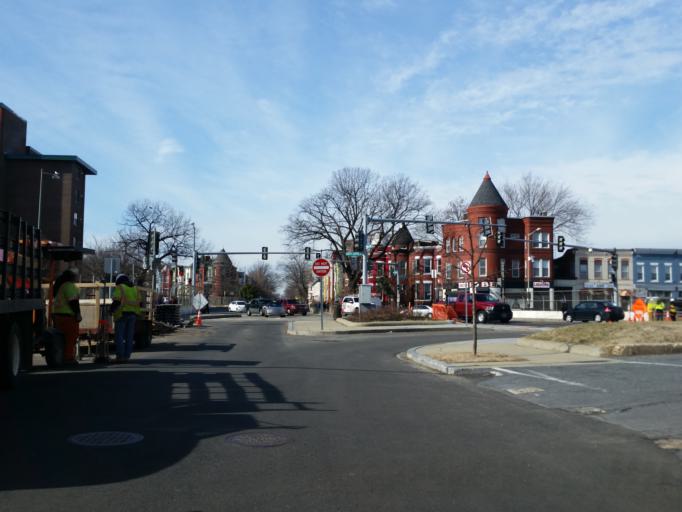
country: US
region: Washington, D.C.
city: Washington, D.C.
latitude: 38.9073
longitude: -77.0083
